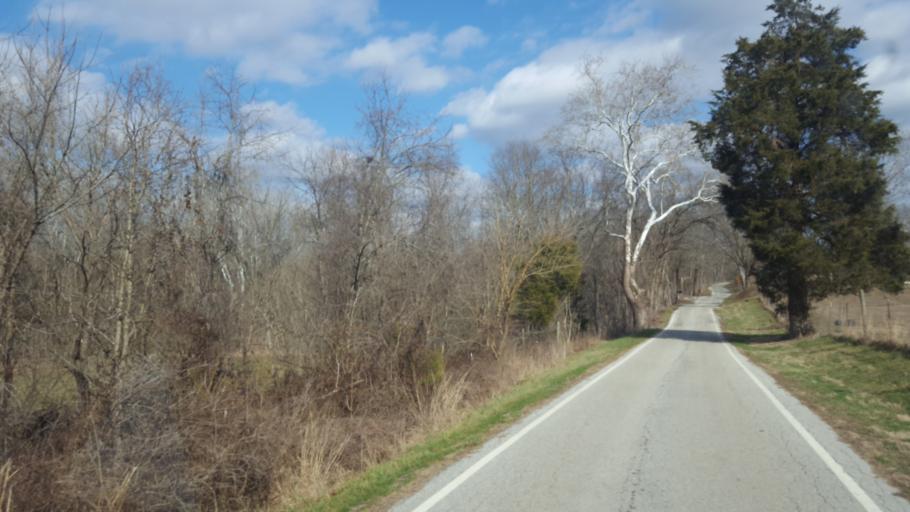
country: US
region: Kentucky
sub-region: Franklin County
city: Frankfort
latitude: 38.3308
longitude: -84.8959
